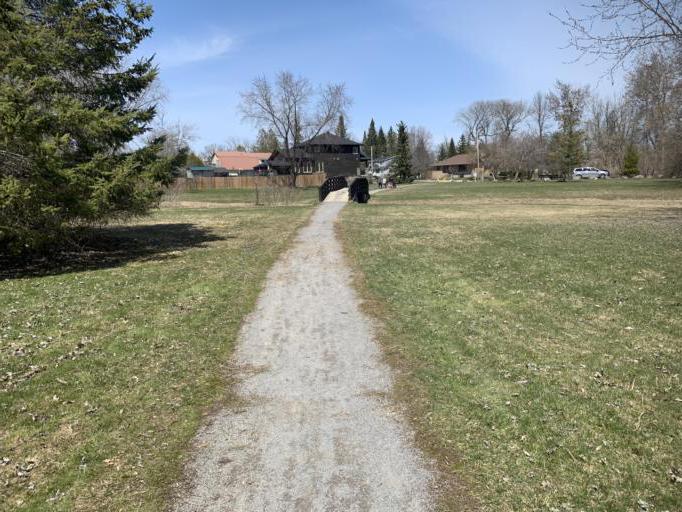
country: CA
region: Ontario
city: Bells Corners
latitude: 45.1873
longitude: -75.8339
